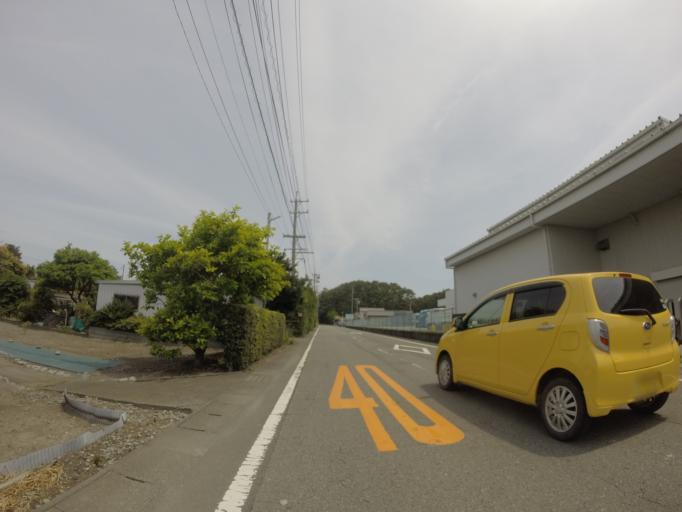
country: JP
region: Shizuoka
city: Yaizu
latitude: 34.8085
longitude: 138.3189
